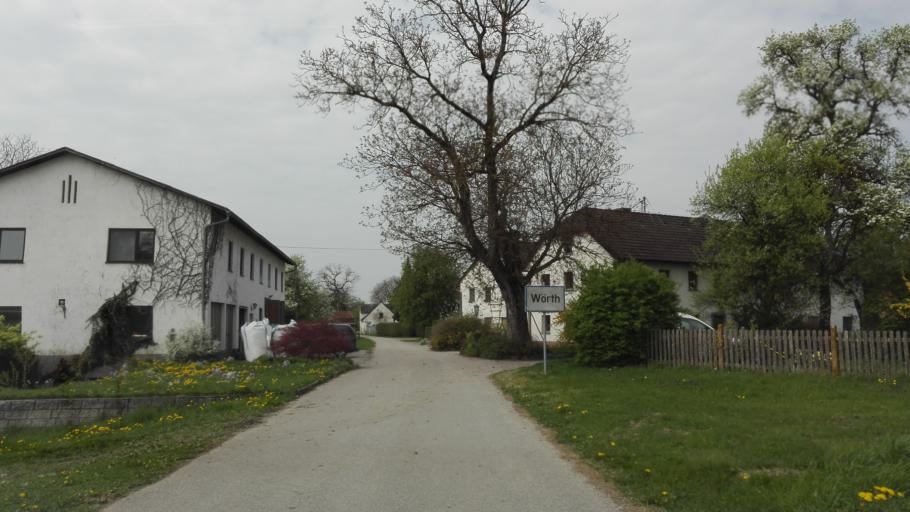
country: AT
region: Lower Austria
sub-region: Politischer Bezirk Amstetten
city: Strengberg
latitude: 48.1804
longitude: 14.6719
